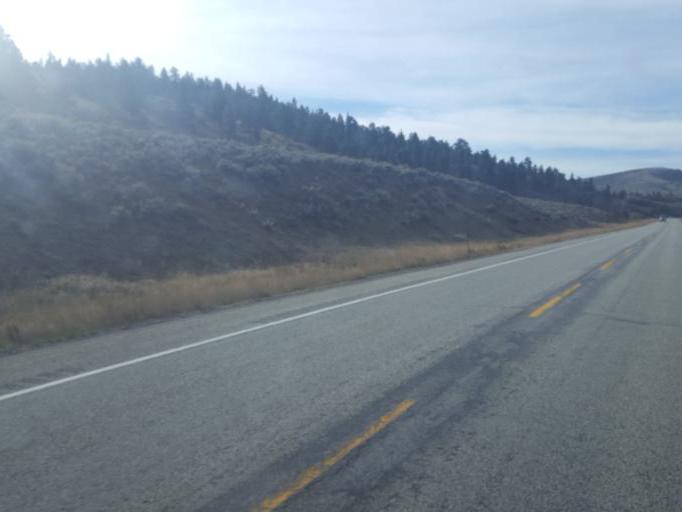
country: US
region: Colorado
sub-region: Costilla County
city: San Luis
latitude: 37.5252
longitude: -105.2982
